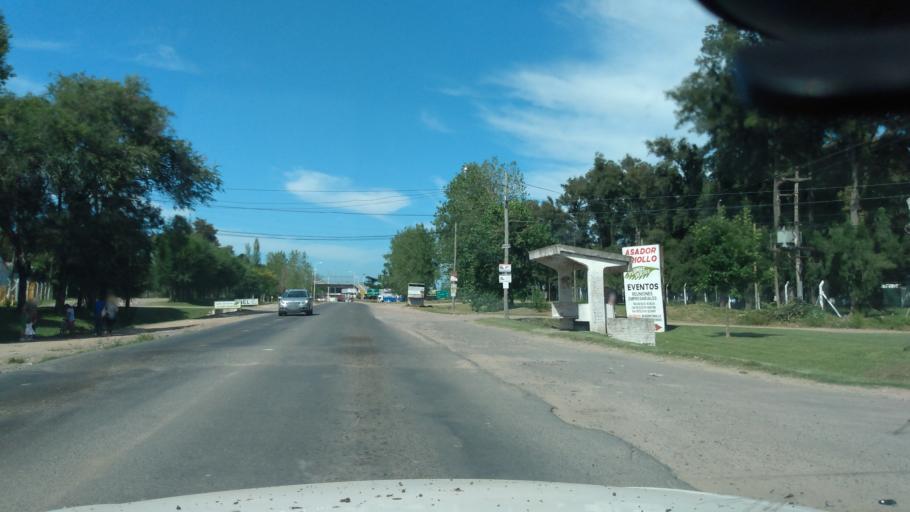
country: AR
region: Buenos Aires
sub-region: Partido de Lujan
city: Lujan
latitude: -34.5481
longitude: -59.1244
